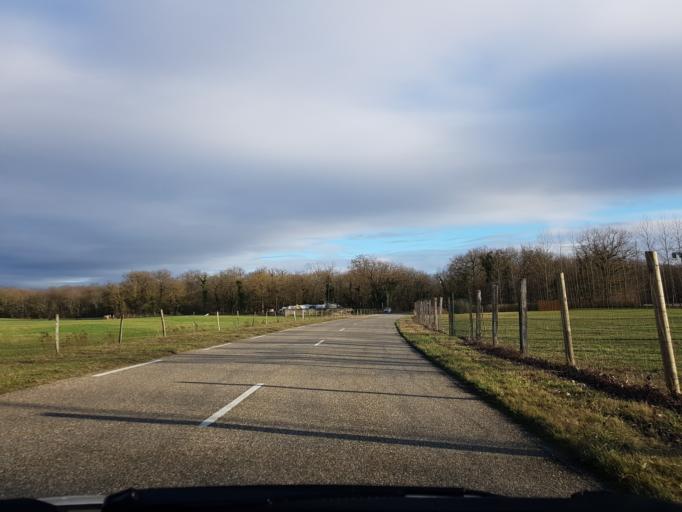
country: FR
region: Alsace
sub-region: Departement du Haut-Rhin
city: Habsheim
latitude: 47.7273
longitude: 7.4362
